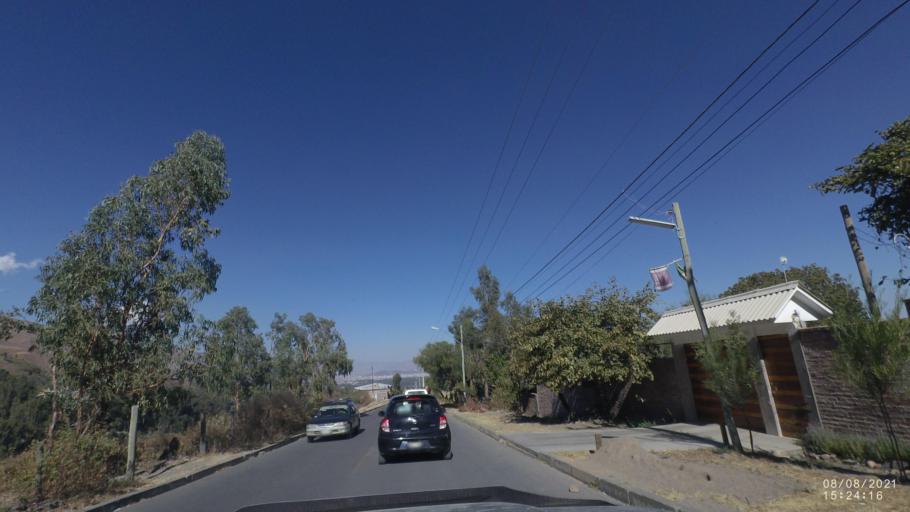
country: BO
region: Cochabamba
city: Cochabamba
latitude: -17.3125
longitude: -66.2890
